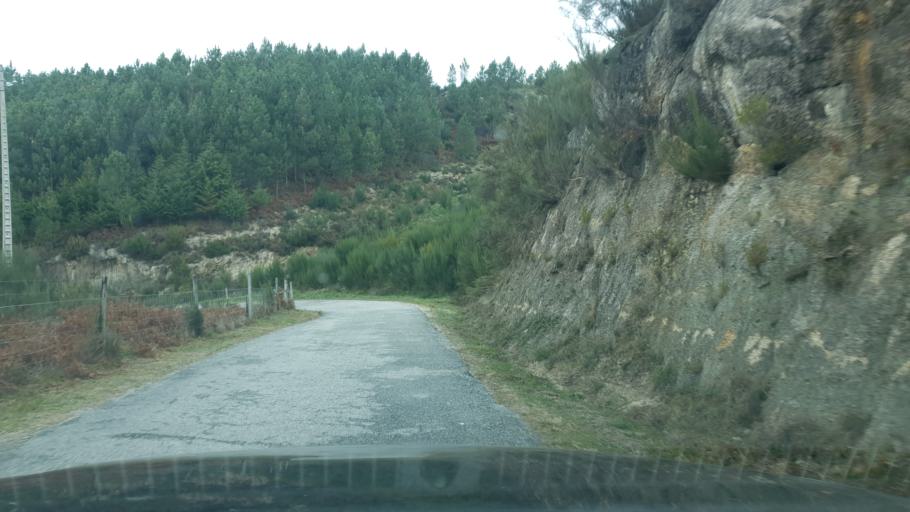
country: PT
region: Viseu
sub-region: Castro Daire
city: Castro Daire
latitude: 40.8783
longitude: -7.9902
